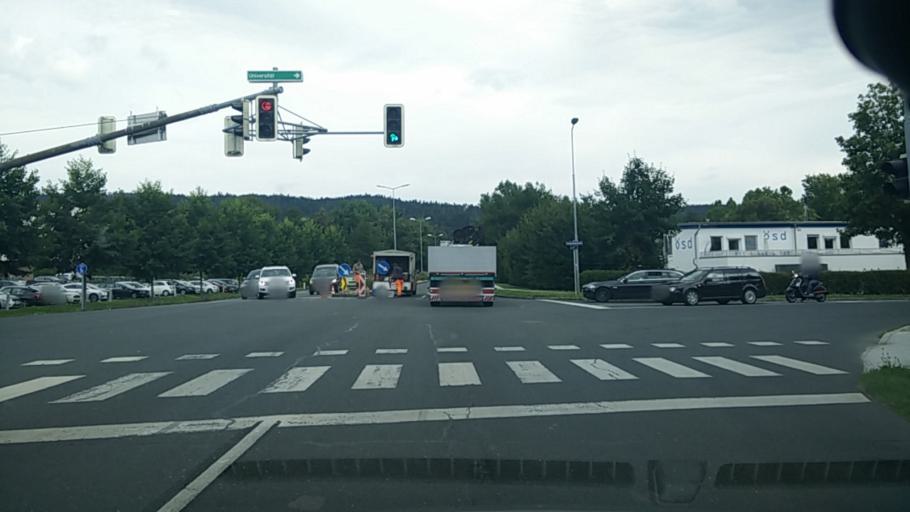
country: AT
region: Carinthia
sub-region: Klagenfurt am Woerthersee
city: Klagenfurt am Woerthersee
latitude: 46.6170
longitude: 14.2616
